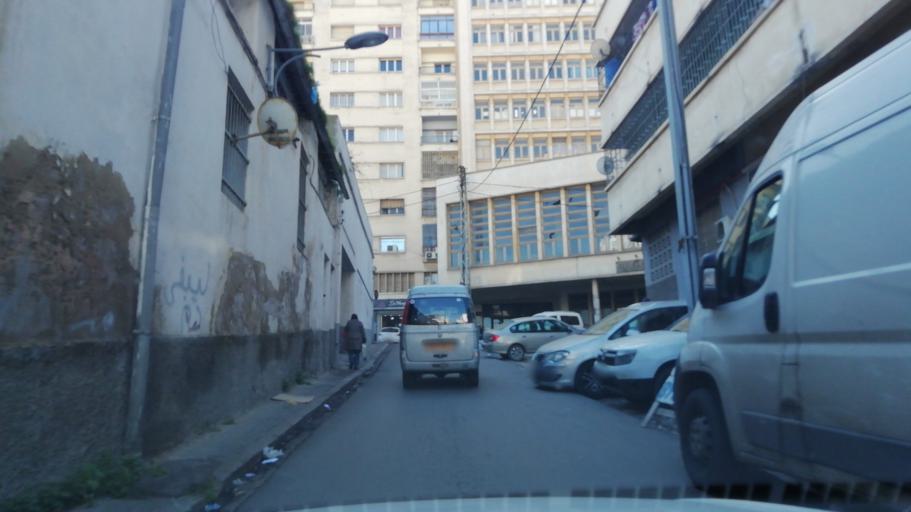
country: DZ
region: Oran
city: Oran
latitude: 35.7030
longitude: -0.6348
